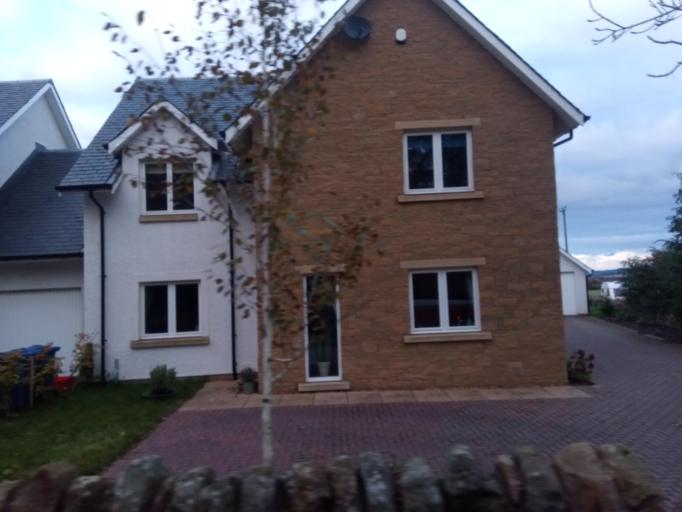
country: GB
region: Scotland
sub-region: Fife
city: Pathhead
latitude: 55.8762
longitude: -3.0045
